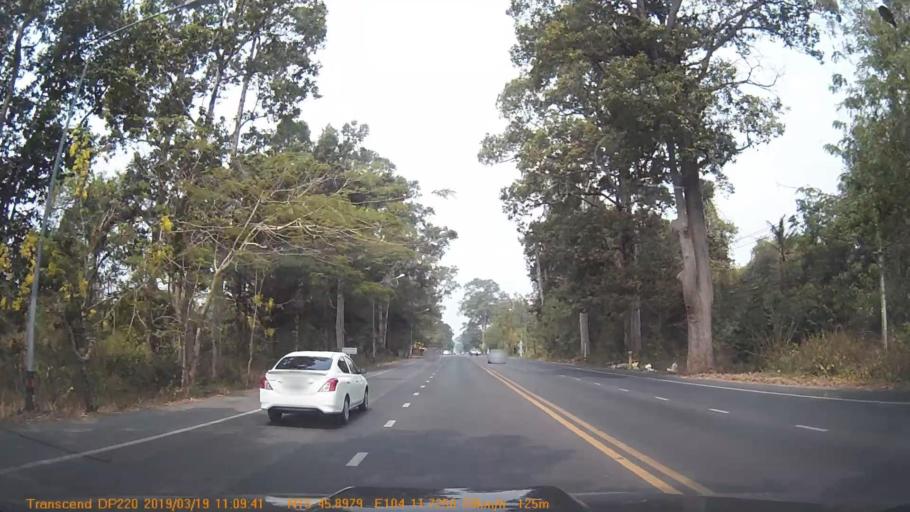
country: TH
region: Yasothon
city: Yasothon
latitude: 15.7651
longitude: 104.1952
